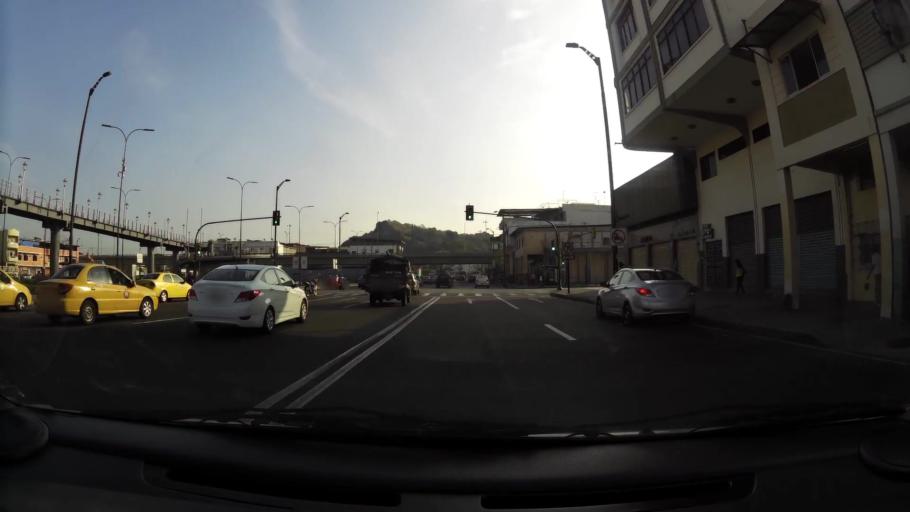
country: EC
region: Guayas
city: Guayaquil
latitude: -2.1862
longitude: -79.8881
